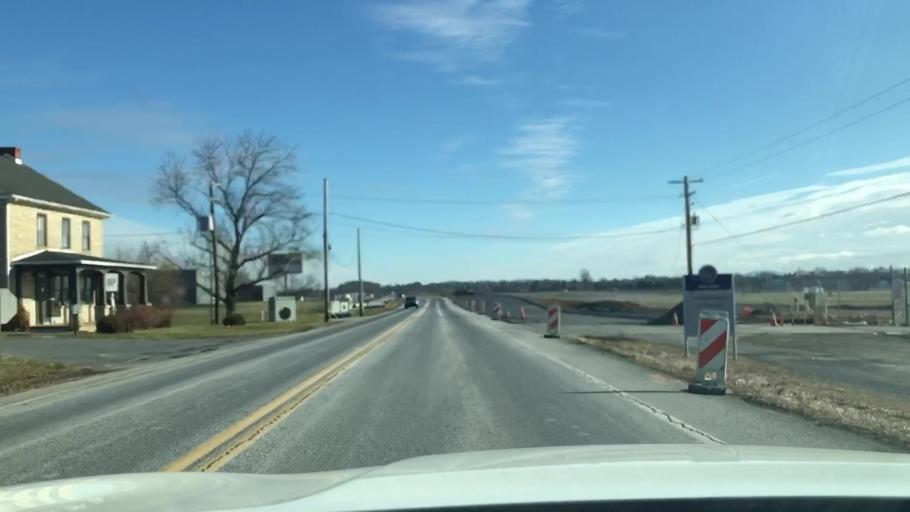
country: US
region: Pennsylvania
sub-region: Lehigh County
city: Catasauqua
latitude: 40.6614
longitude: -75.4335
